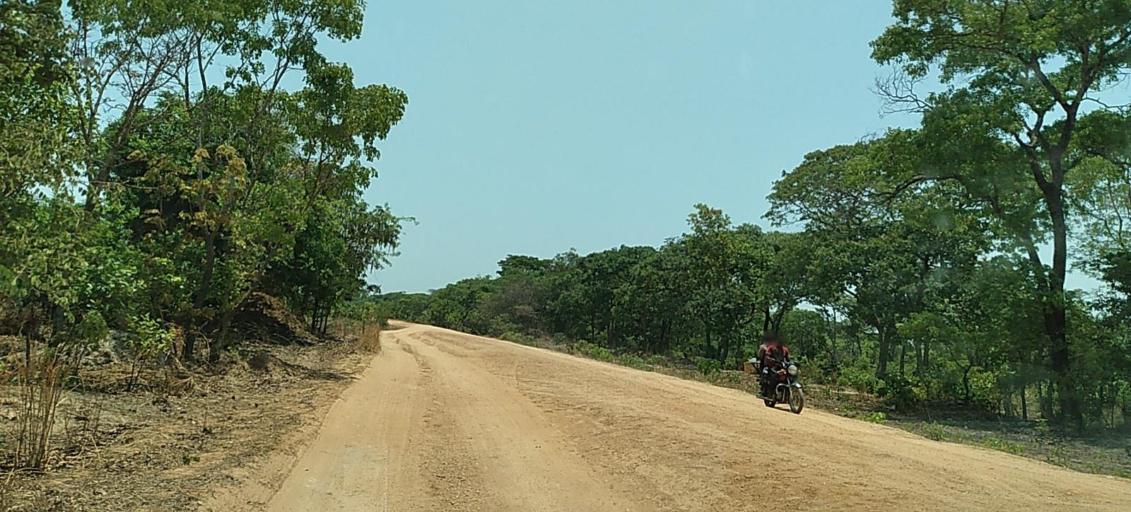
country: ZM
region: Copperbelt
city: Mpongwe
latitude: -13.8066
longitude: 27.8565
